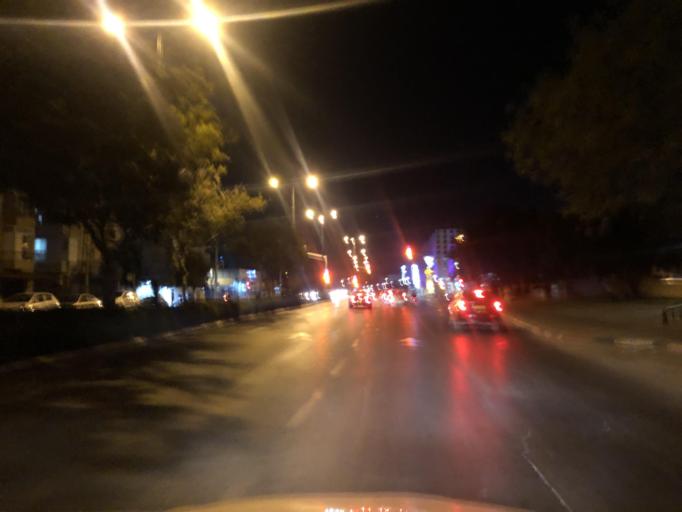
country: IL
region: Tel Aviv
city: Yafo
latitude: 32.0489
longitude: 34.7747
